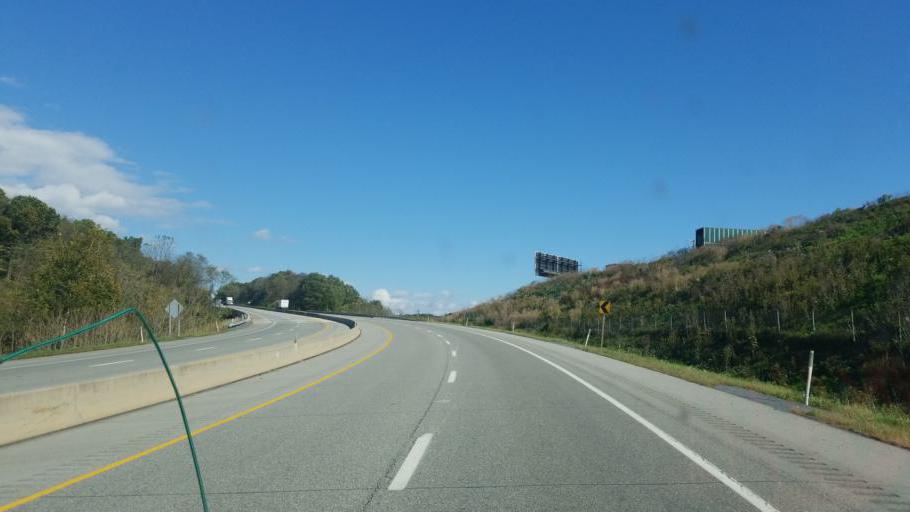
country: US
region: Pennsylvania
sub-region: Bedford County
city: Everett
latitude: 40.0112
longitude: -78.3809
